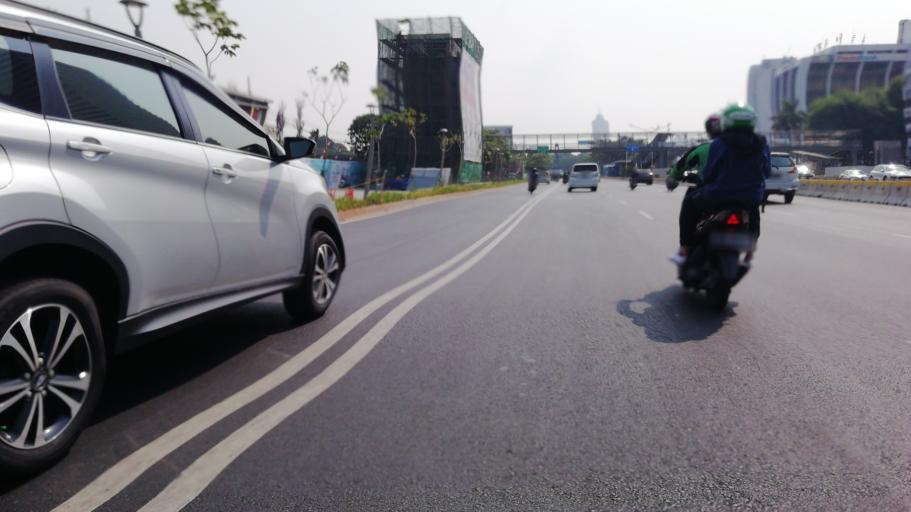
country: ID
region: Jakarta Raya
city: Jakarta
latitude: -6.2271
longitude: 106.8026
